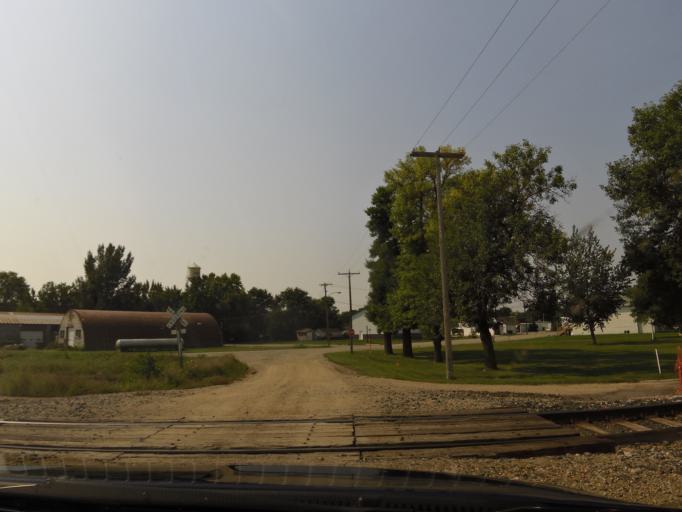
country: US
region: North Dakota
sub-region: Ransom County
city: Sheldon
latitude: 46.2671
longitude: -97.1284
